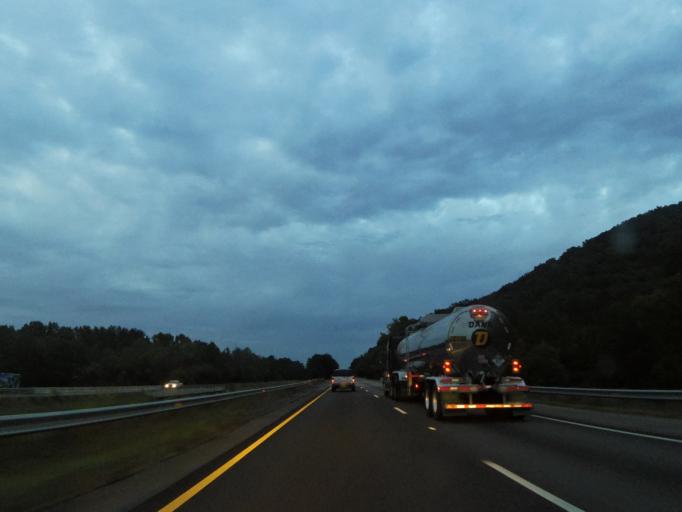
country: US
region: Alabama
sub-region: Etowah County
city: Whitesboro
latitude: 34.1511
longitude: -85.9842
